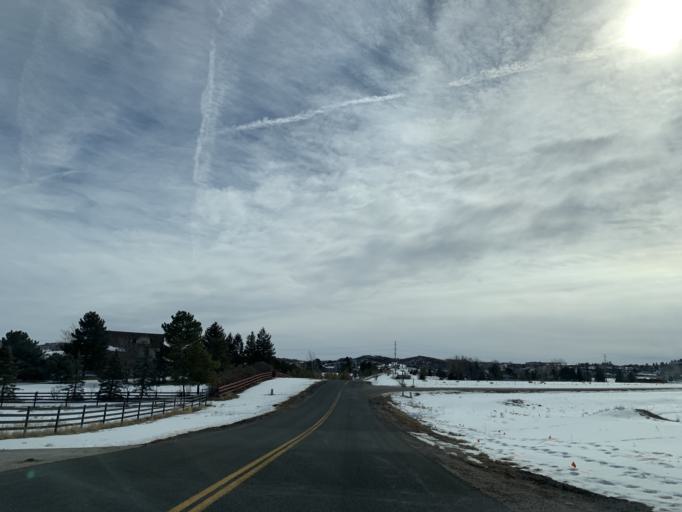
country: US
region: Colorado
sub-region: Douglas County
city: Carriage Club
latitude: 39.5184
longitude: -104.9100
